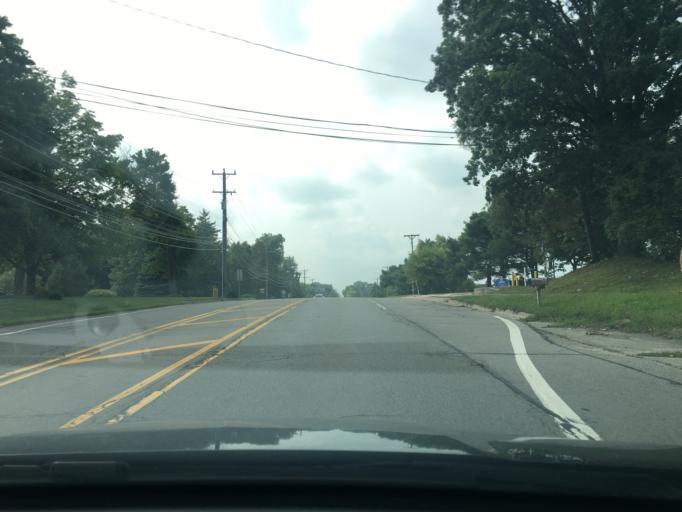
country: US
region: Michigan
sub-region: Oakland County
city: Rochester Hills
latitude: 42.6348
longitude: -83.1815
